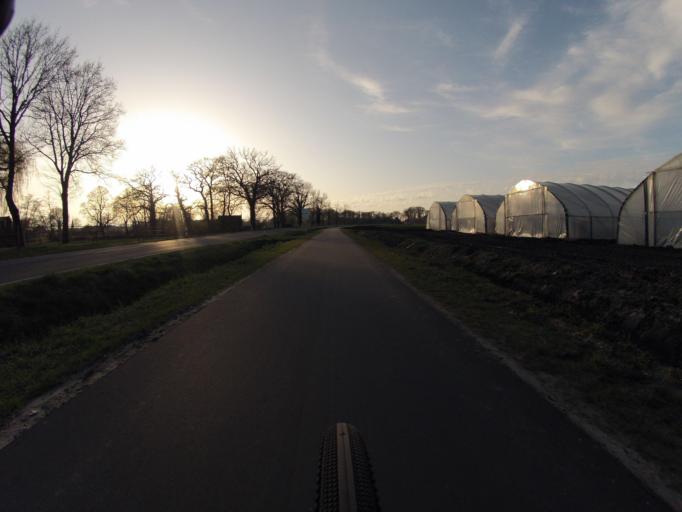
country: DE
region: North Rhine-Westphalia
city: Ibbenburen
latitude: 52.2258
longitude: 7.7206
